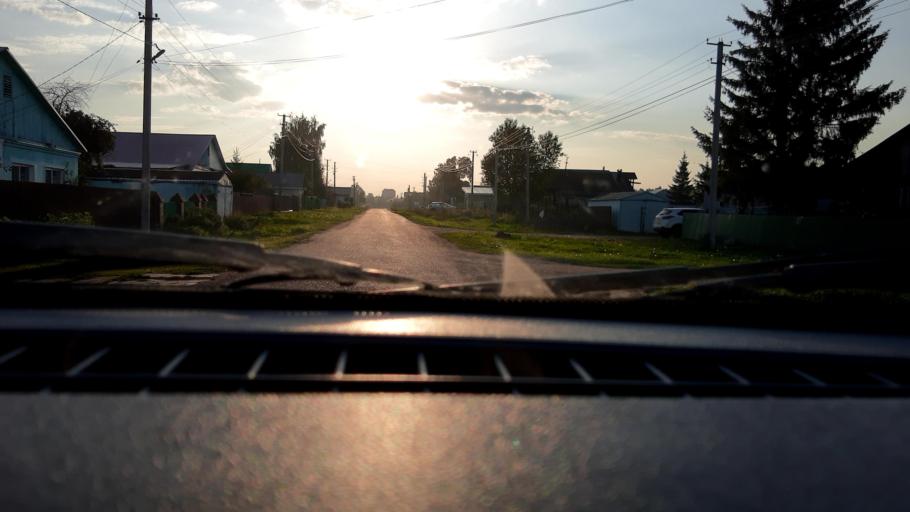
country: RU
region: Bashkortostan
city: Mikhaylovka
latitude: 54.8903
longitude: 55.8983
